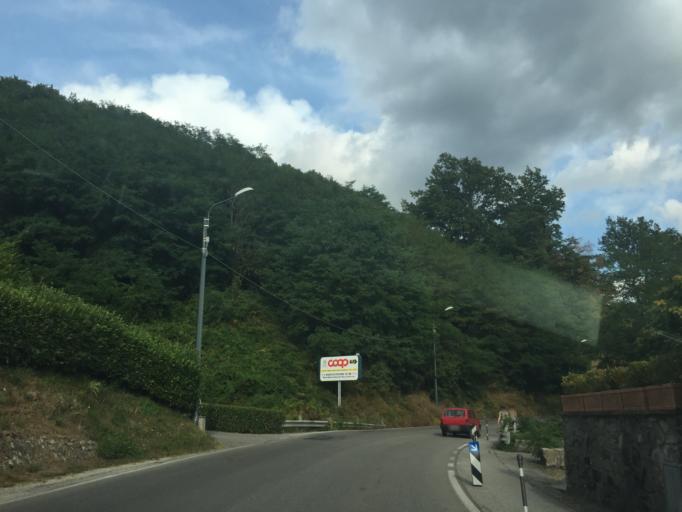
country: IT
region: Tuscany
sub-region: Provincia di Pistoia
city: San Marcello Pistoiese
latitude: 44.0566
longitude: 10.7840
